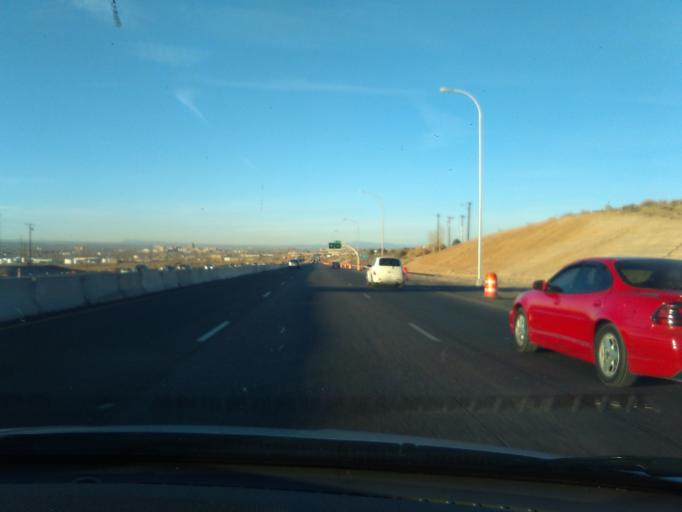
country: US
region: New Mexico
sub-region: Bernalillo County
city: South Valley
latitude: 35.0269
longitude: -106.6381
